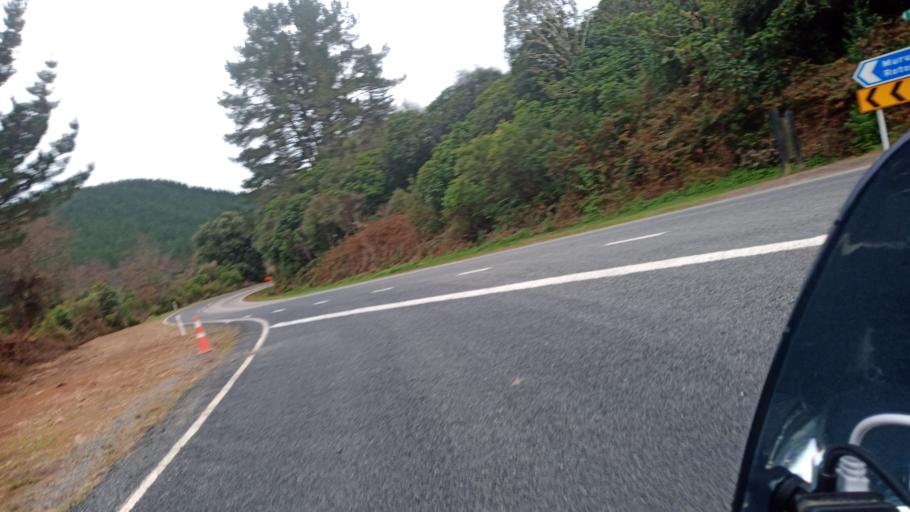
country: NZ
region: Bay of Plenty
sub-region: Whakatane District
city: Murupara
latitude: -38.5862
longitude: 176.7813
